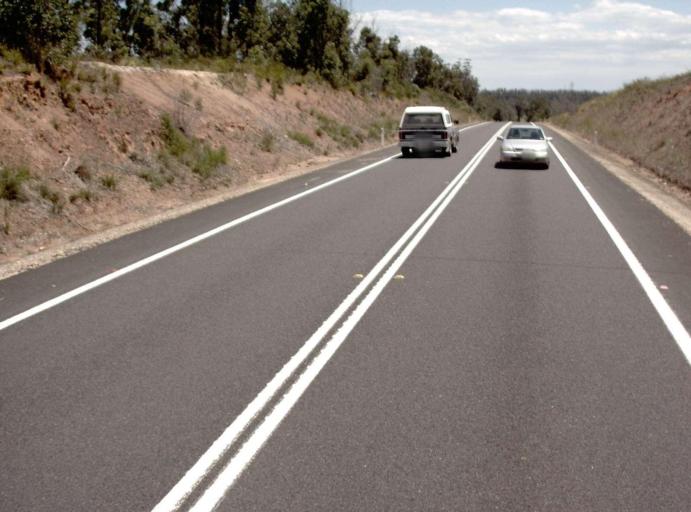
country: AU
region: Victoria
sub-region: East Gippsland
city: Lakes Entrance
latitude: -37.7523
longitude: 148.2879
